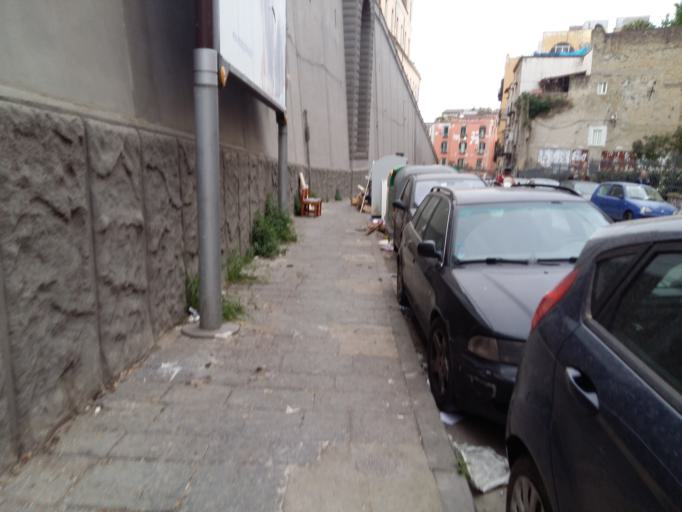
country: IT
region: Campania
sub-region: Provincia di Napoli
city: Napoli
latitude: 40.8537
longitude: 14.2438
